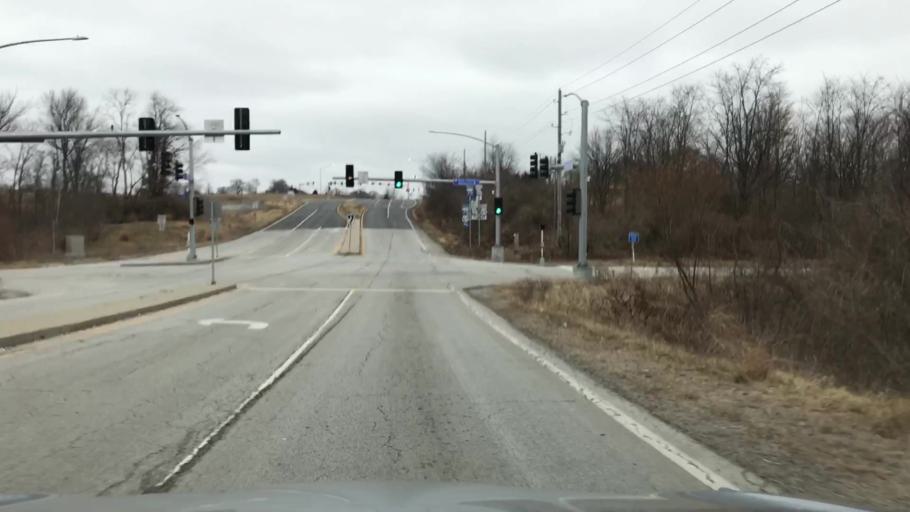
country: US
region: Missouri
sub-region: Clay County
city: Liberty
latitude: 39.2787
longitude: -94.4166
